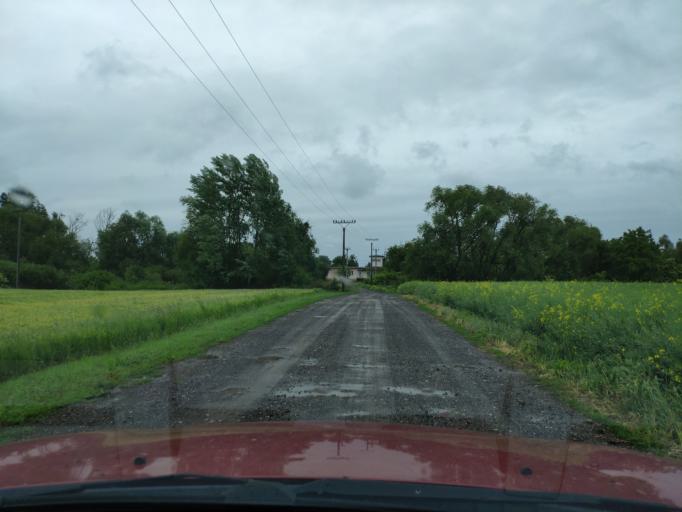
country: SK
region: Kosicky
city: Cierna nad Tisou
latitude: 48.4252
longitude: 22.0823
